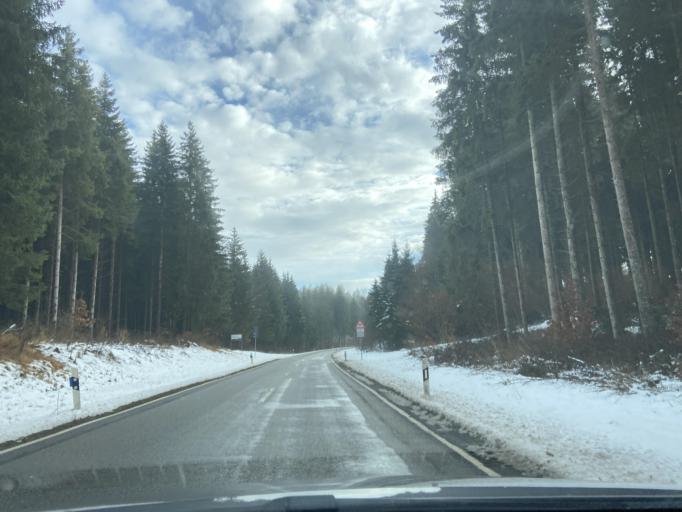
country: DE
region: Baden-Wuerttemberg
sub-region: Tuebingen Region
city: Pfronstetten
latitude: 48.2423
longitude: 9.3472
